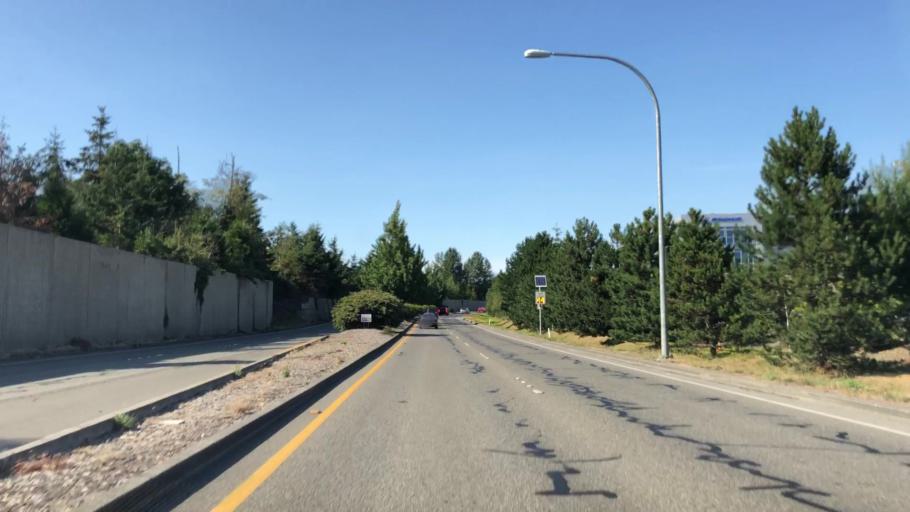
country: US
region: Washington
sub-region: Snohomish County
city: Mukilteo
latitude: 47.9185
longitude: -122.2926
